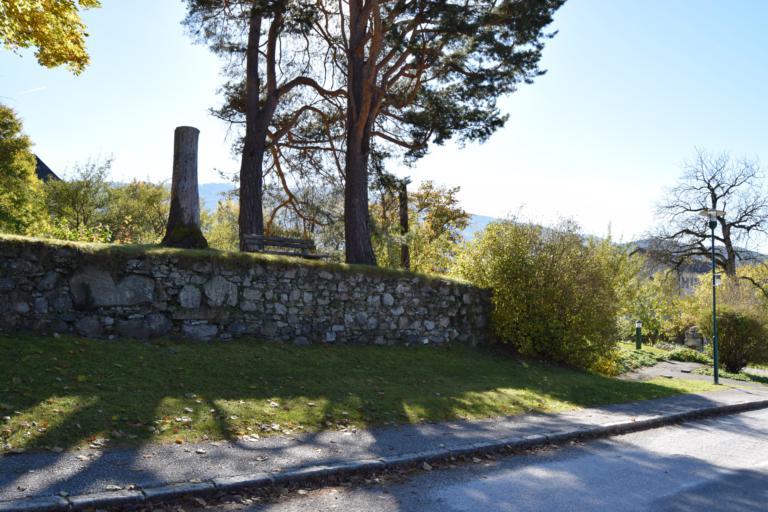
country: AT
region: Styria
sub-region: Politischer Bezirk Liezen
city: Irdning
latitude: 47.5065
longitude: 14.1044
